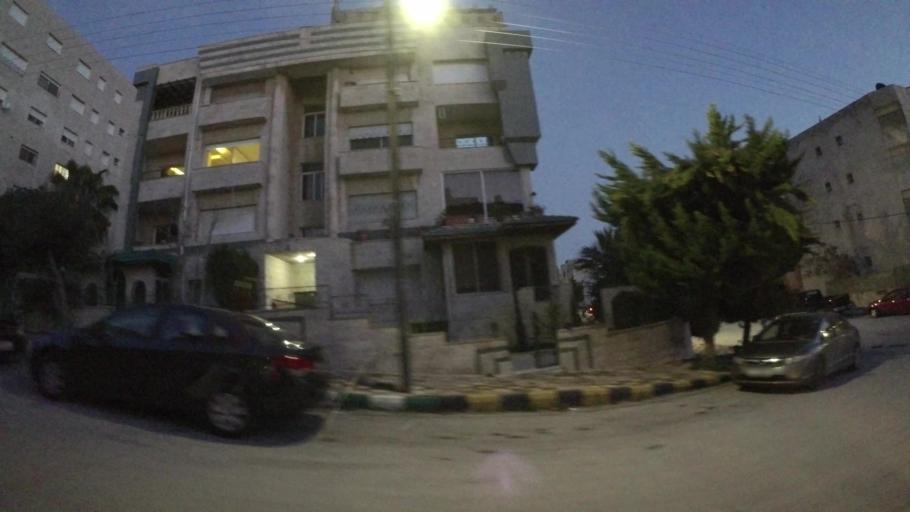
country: JO
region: Amman
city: Al Jubayhah
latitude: 31.9812
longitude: 35.8820
